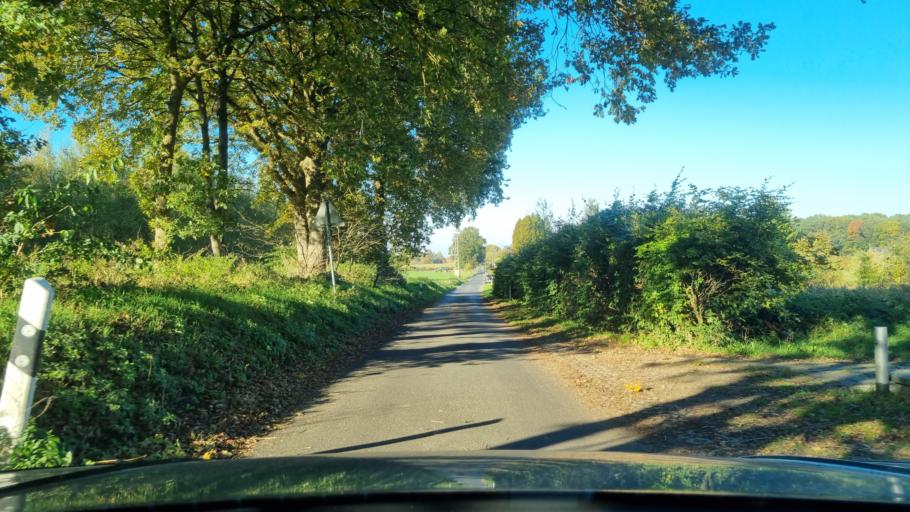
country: DE
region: North Rhine-Westphalia
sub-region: Regierungsbezirk Dusseldorf
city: Kranenburg
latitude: 51.7770
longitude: 6.0634
